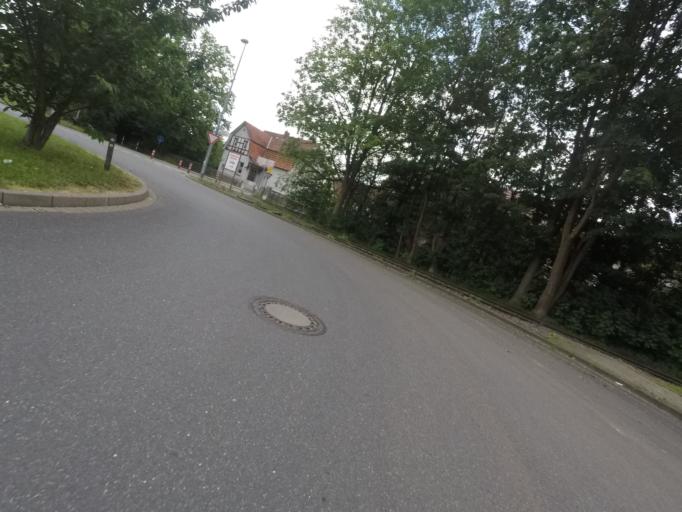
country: DE
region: North Rhine-Westphalia
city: Enger
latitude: 52.1374
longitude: 8.5554
